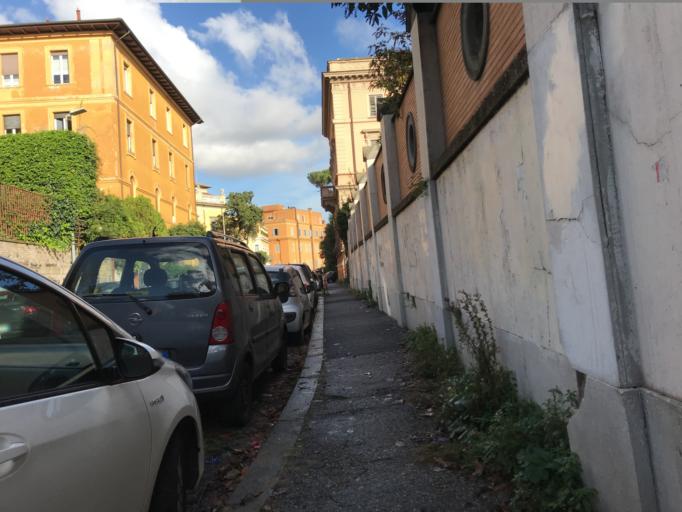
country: IT
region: Latium
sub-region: Citta metropolitana di Roma Capitale
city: Rome
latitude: 41.9100
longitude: 12.5067
